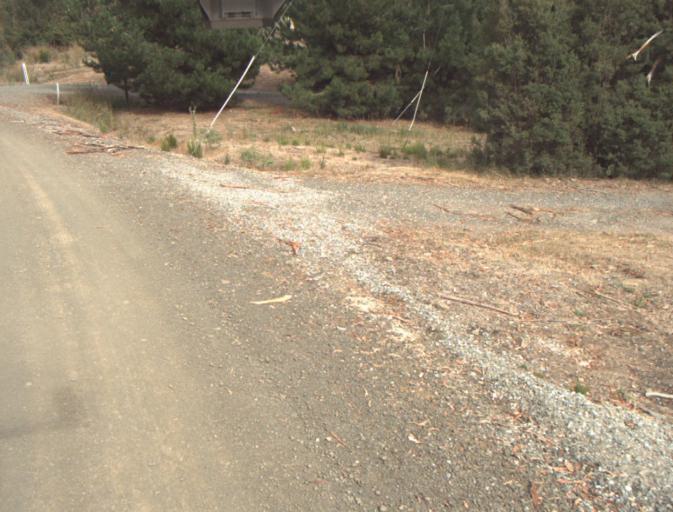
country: AU
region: Tasmania
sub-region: Launceston
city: Mayfield
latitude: -41.2744
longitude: 147.2215
